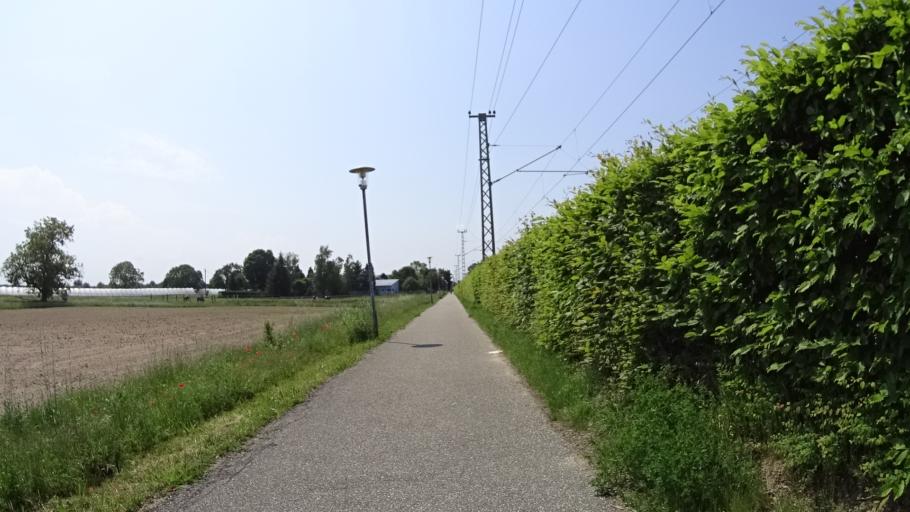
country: DE
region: Baden-Wuerttemberg
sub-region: Karlsruhe Region
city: Eggenstein-Leopoldshafen
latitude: 49.0784
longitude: 8.3992
